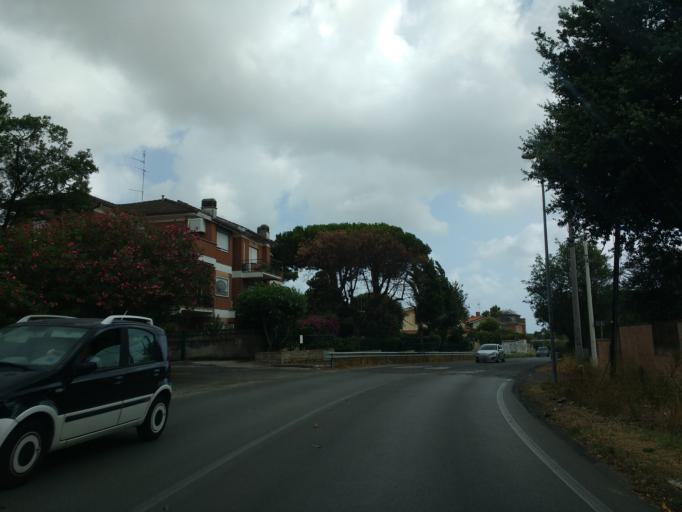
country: IT
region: Latium
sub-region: Citta metropolitana di Roma Capitale
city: Anzio
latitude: 41.4808
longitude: 12.6042
